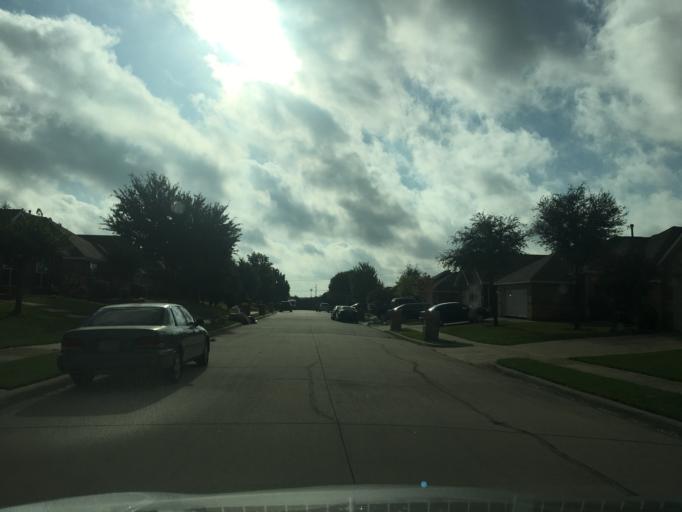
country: US
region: Texas
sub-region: Dallas County
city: Sachse
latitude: 32.9662
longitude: -96.5976
